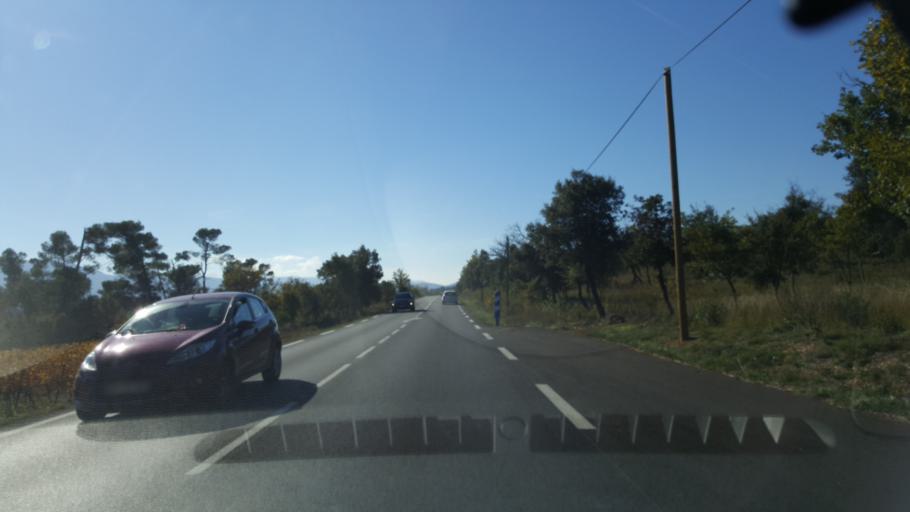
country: FR
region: Provence-Alpes-Cote d'Azur
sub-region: Departement du Var
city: Rougiers
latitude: 43.4197
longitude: 5.8347
